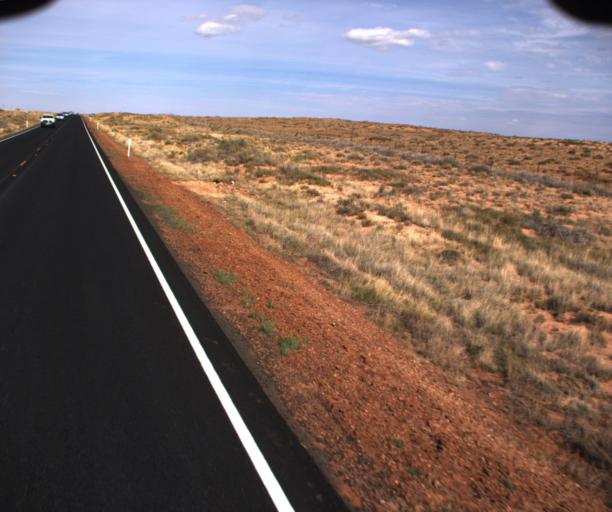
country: US
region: Arizona
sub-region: Apache County
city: Chinle
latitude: 36.0154
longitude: -109.6051
